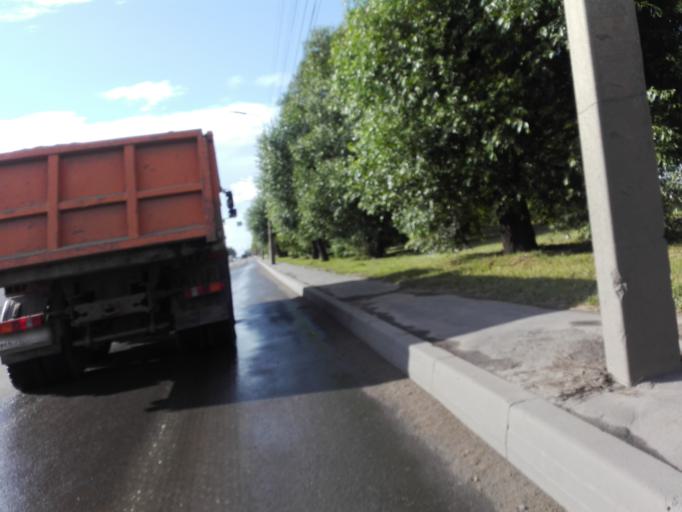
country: RU
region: Orjol
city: Orel
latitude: 52.9892
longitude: 36.1193
